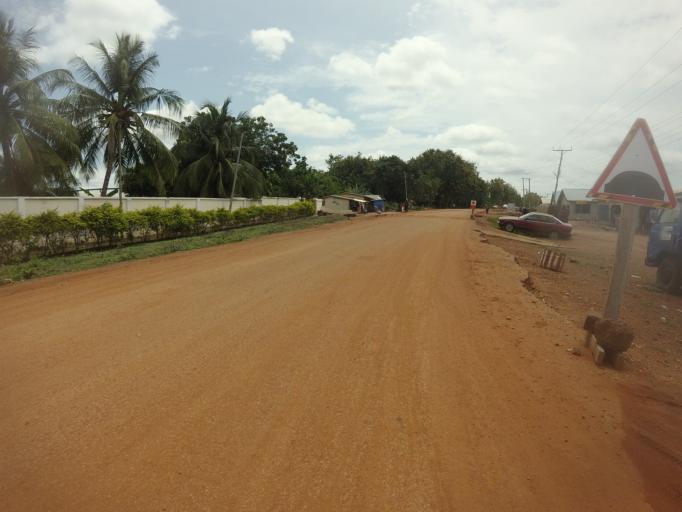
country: GH
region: Volta
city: Ho
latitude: 6.5688
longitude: 0.3989
